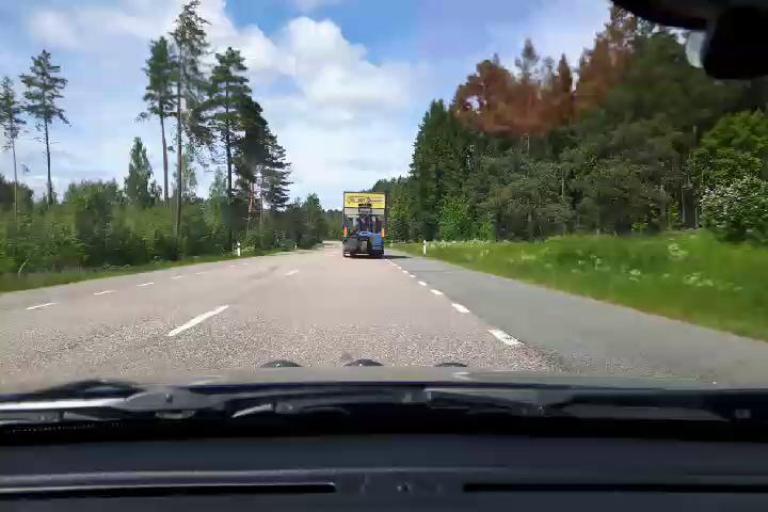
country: SE
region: Uppsala
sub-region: Osthammars Kommun
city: Bjorklinge
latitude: 60.1034
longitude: 17.5499
